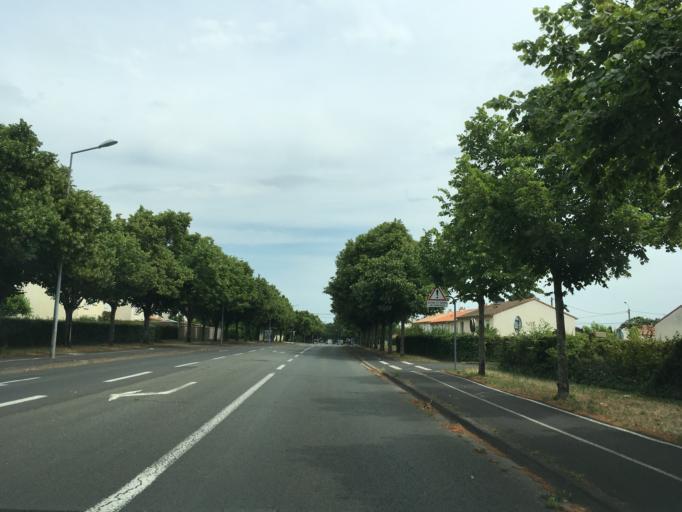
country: FR
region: Poitou-Charentes
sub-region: Departement des Deux-Sevres
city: Niort
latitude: 46.3111
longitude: -0.4762
